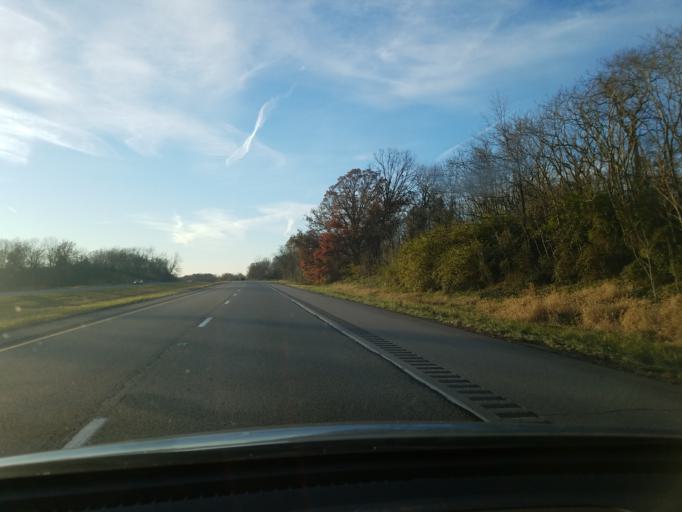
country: US
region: Indiana
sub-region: Warrick County
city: Boonville
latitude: 38.2018
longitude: -87.2026
